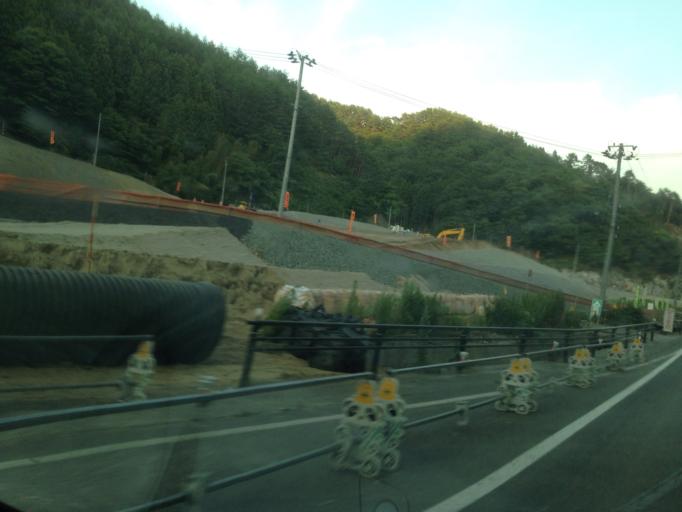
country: JP
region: Iwate
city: Kamaishi
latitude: 39.3114
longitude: 141.8867
